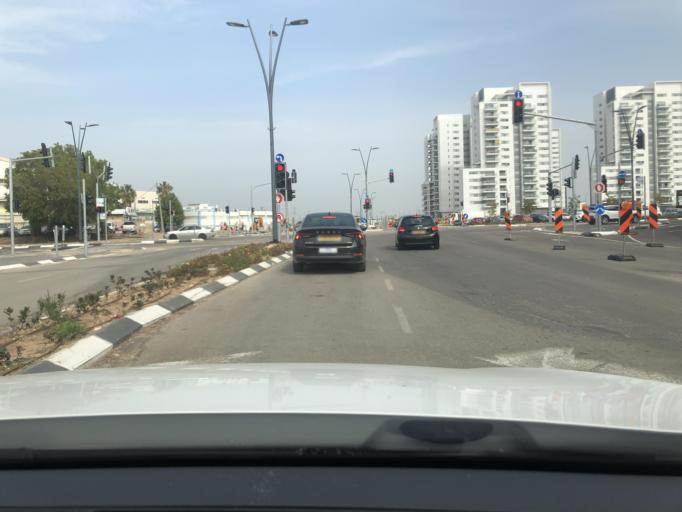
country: IL
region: Central District
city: Rosh Ha'Ayin
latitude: 32.1046
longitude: 34.9417
